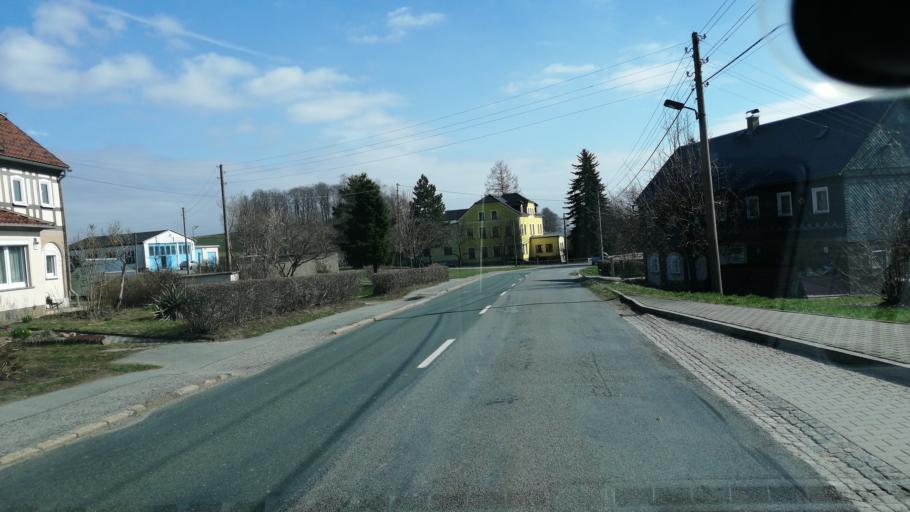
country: DE
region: Saxony
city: Schonbach
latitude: 51.0829
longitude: 14.5688
